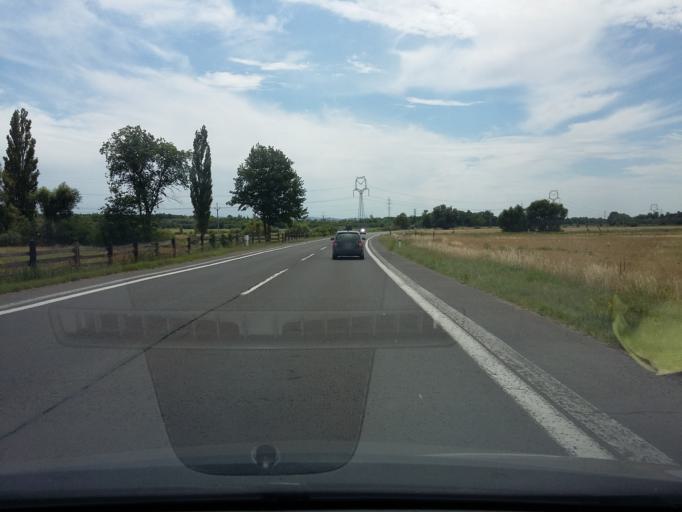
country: SK
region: Bratislavsky
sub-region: Okres Malacky
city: Malacky
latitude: 48.4874
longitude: 17.0111
